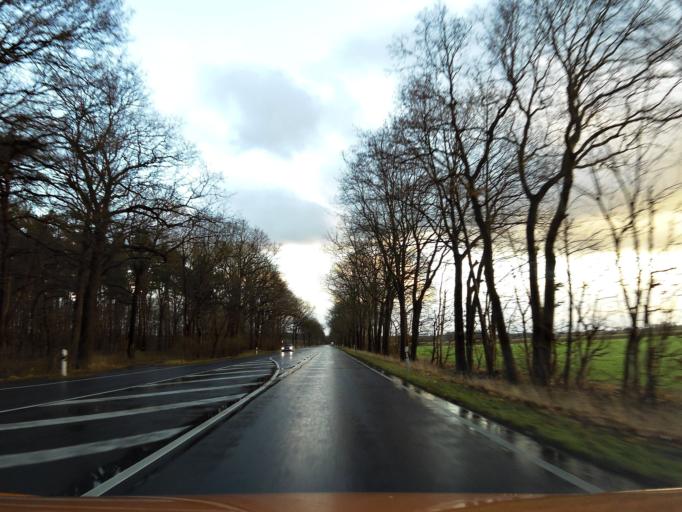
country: DE
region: Lower Saxony
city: Meinersen
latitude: 52.4228
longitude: 10.3421
